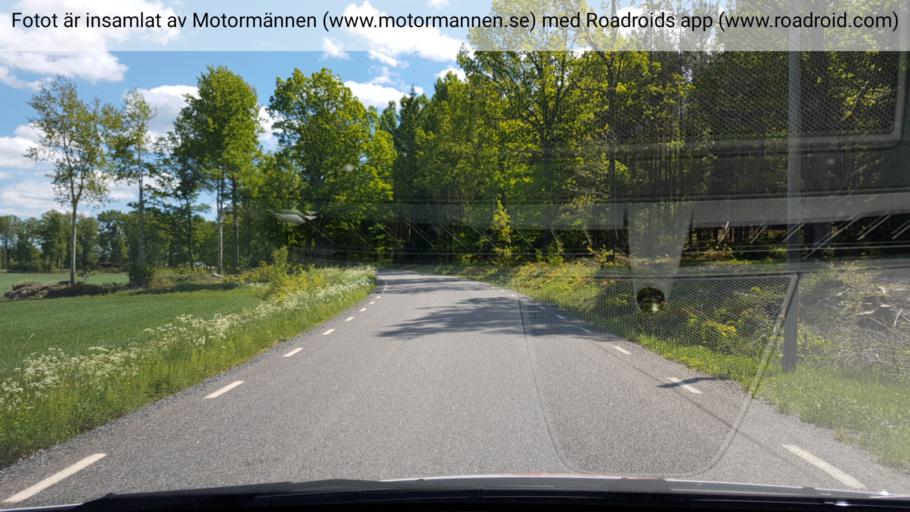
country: SE
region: Kalmar
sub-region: Vasterviks Kommun
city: Forserum
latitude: 57.9698
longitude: 16.6172
